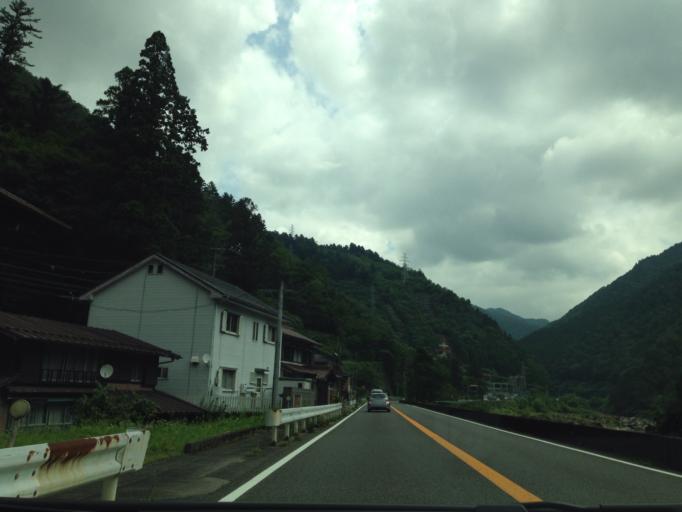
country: JP
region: Gifu
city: Gujo
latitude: 35.7320
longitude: 137.1991
